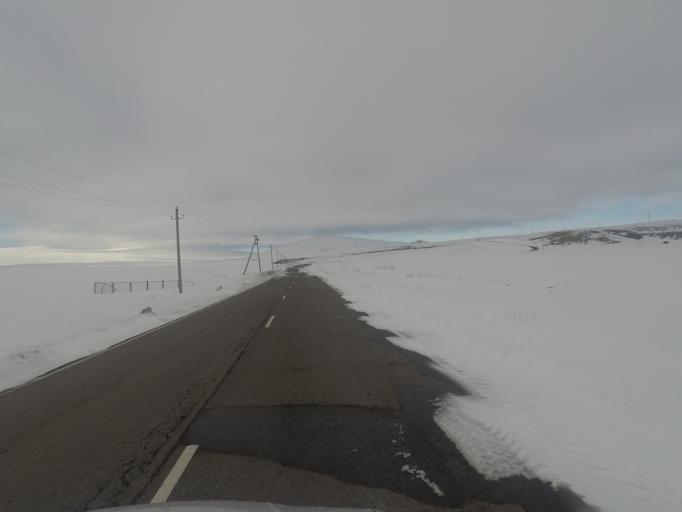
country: GE
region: Samtskhe-Javakheti
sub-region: Ninotsminda
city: Ninotsminda
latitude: 41.4310
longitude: 43.8379
